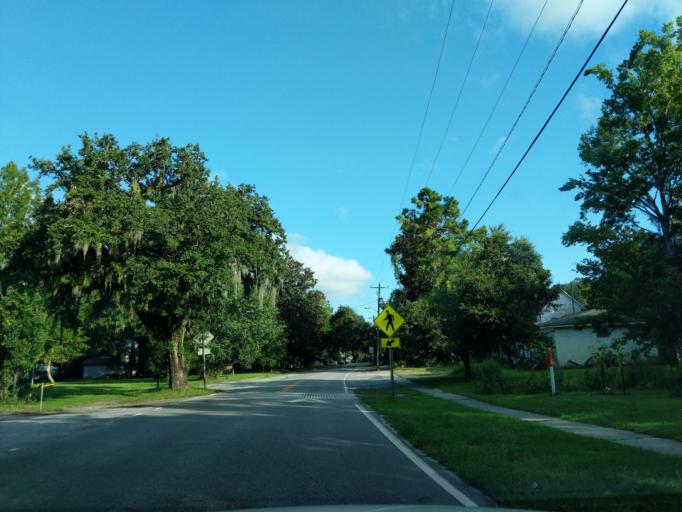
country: US
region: South Carolina
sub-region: Charleston County
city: Awendaw
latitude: 33.0919
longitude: -79.4640
